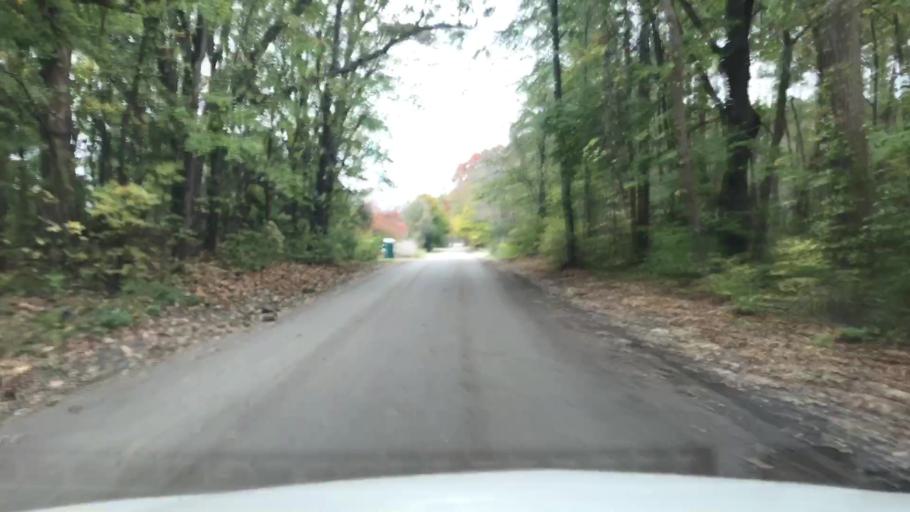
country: US
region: Michigan
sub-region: Oakland County
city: Rochester
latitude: 42.7122
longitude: -83.1251
